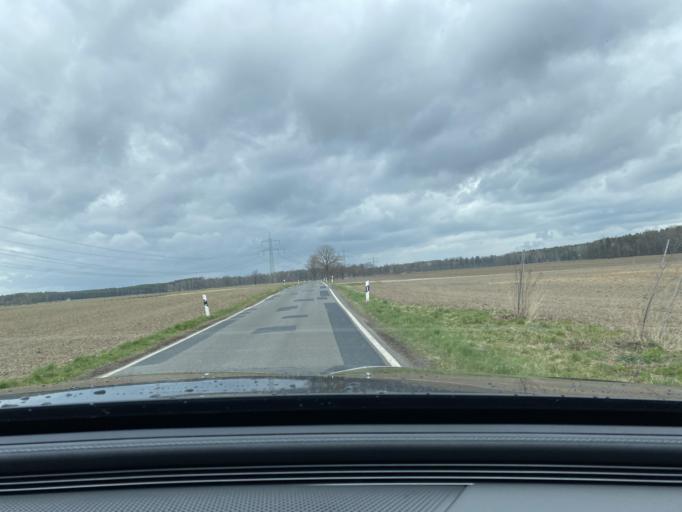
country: DE
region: Saxony
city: Grossdubrau
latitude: 51.3123
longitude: 14.4633
